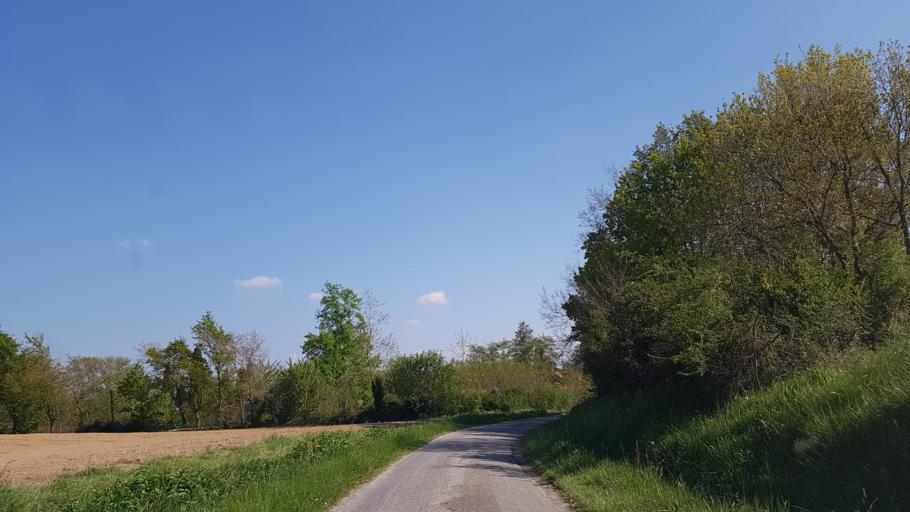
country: FR
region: Midi-Pyrenees
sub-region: Departement de l'Ariege
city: La Tour-du-Crieu
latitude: 43.0973
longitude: 1.7176
